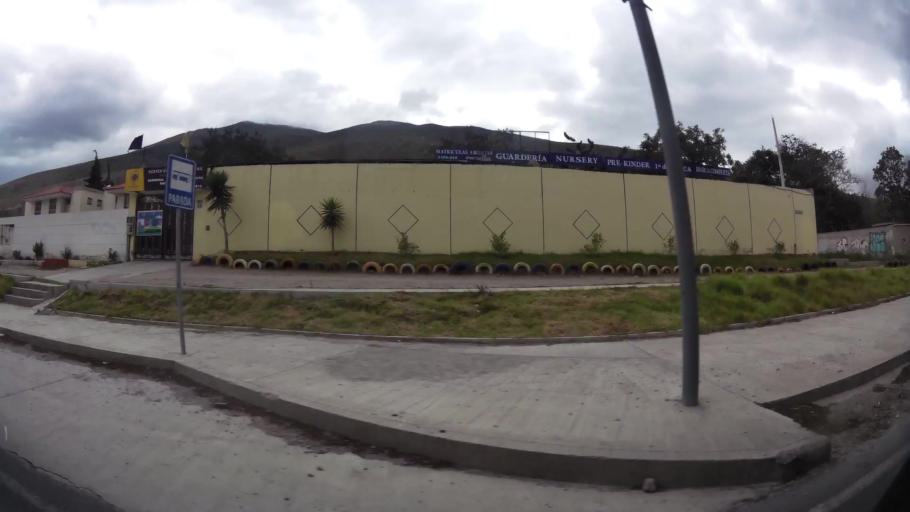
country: EC
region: Pichincha
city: Quito
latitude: -0.0156
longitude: -78.4531
